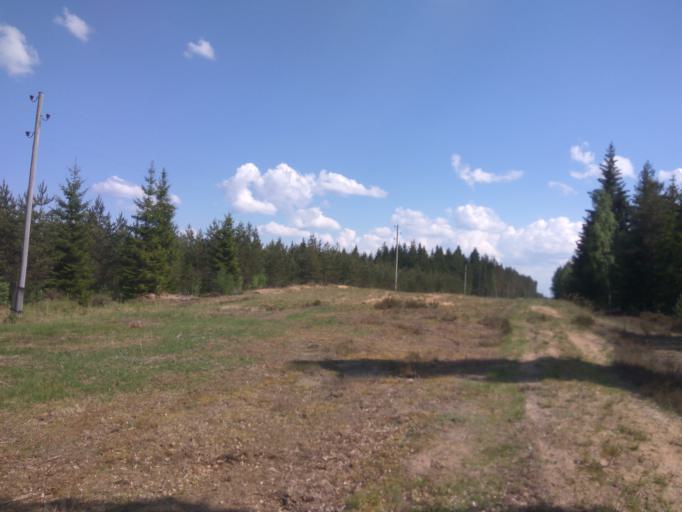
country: LV
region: Kuldigas Rajons
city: Kuldiga
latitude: 57.1853
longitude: 21.9927
